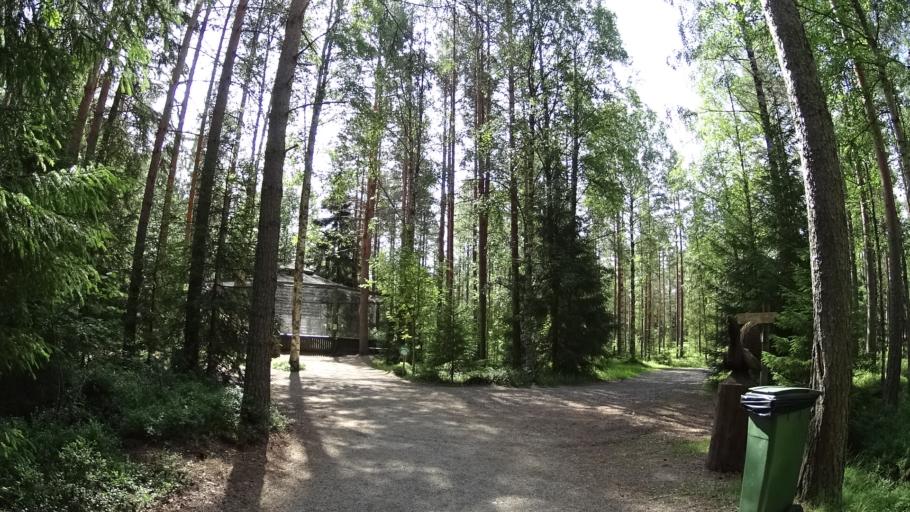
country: FI
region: Southern Ostrobothnia
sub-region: Kuusiokunnat
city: AEhtaeri
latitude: 62.5412
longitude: 24.1770
